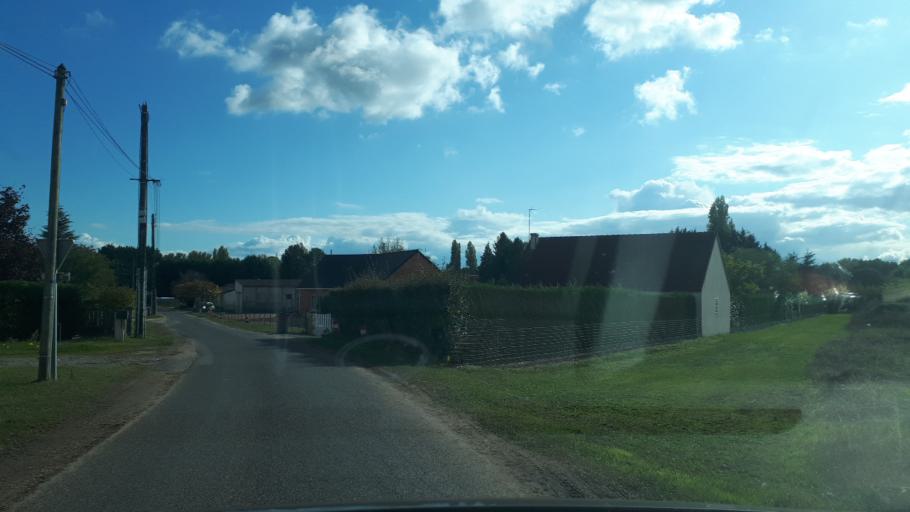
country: FR
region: Centre
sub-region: Departement du Loir-et-Cher
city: Thesee
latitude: 47.3215
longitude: 1.3196
